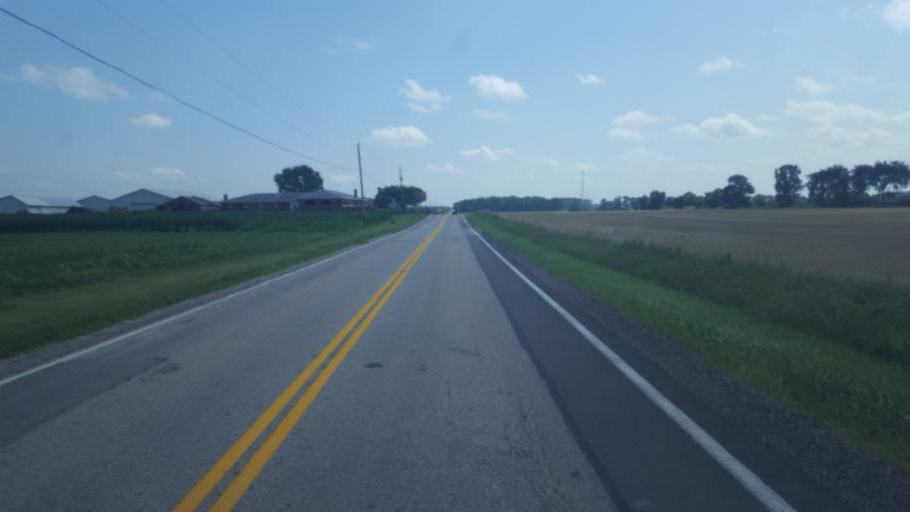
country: US
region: Ohio
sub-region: Huron County
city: Bellevue
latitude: 41.2242
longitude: -82.8389
